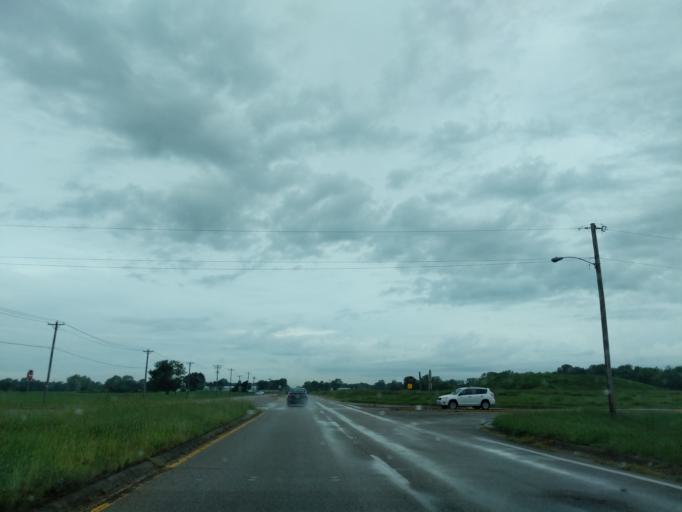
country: US
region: Illinois
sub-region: Saint Clair County
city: Fairmont City
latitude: 38.6589
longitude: -90.0659
